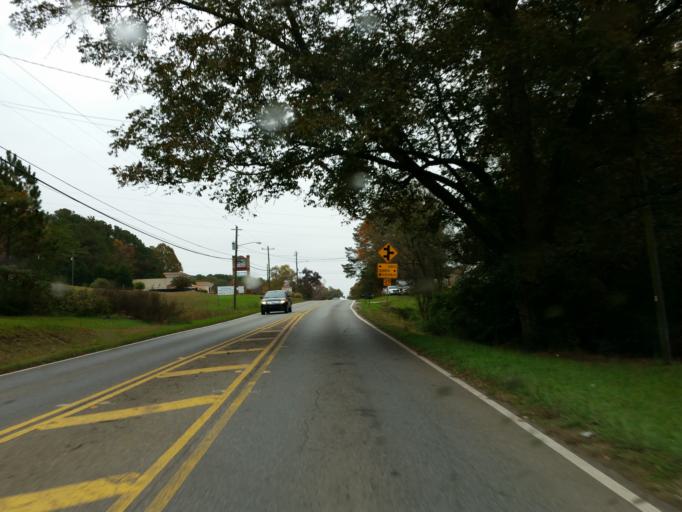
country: US
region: Georgia
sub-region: Pickens County
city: Jasper
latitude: 34.4656
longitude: -84.4482
